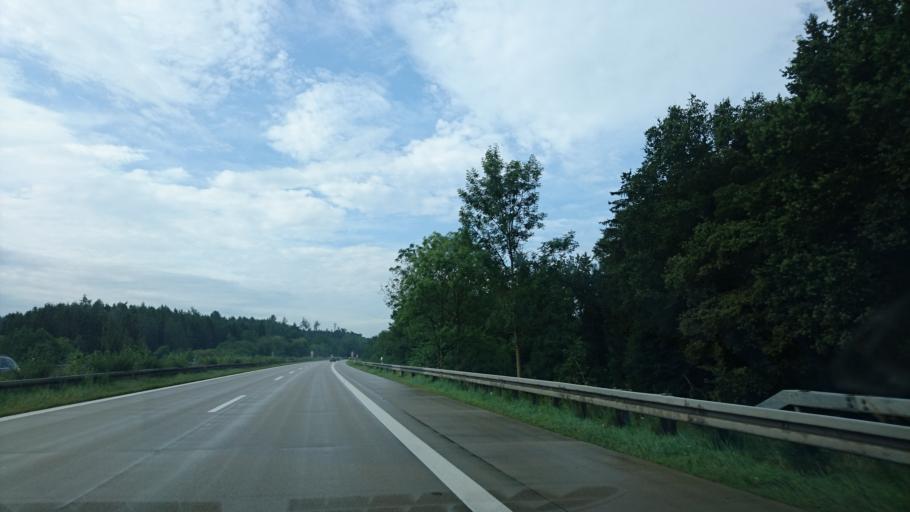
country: DE
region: Bavaria
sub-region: Lower Bavaria
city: Bad Abbach
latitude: 48.9120
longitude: 12.0870
